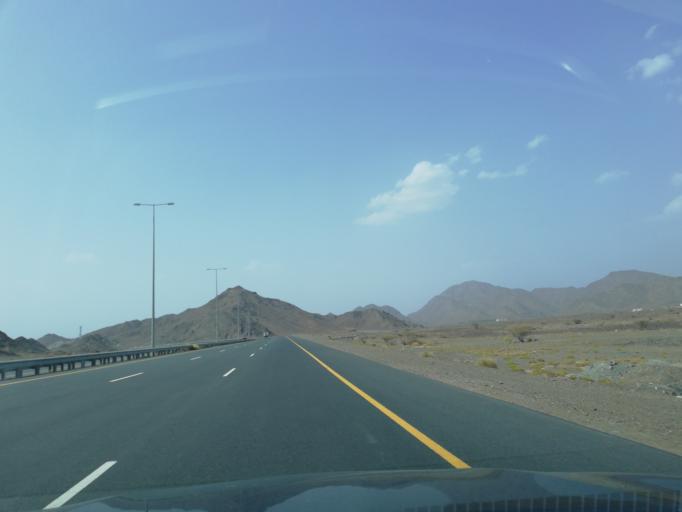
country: OM
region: Ash Sharqiyah
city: Ibra'
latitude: 22.9572
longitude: 58.2453
